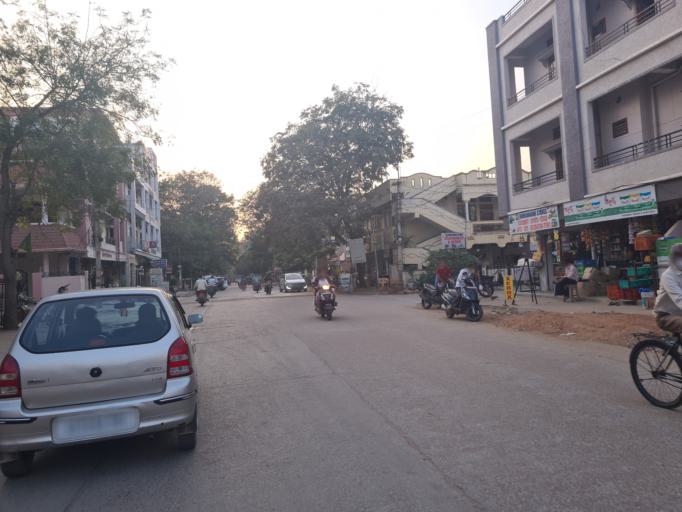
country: IN
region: Telangana
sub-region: Medak
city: Serilingampalle
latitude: 17.4779
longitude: 78.2896
